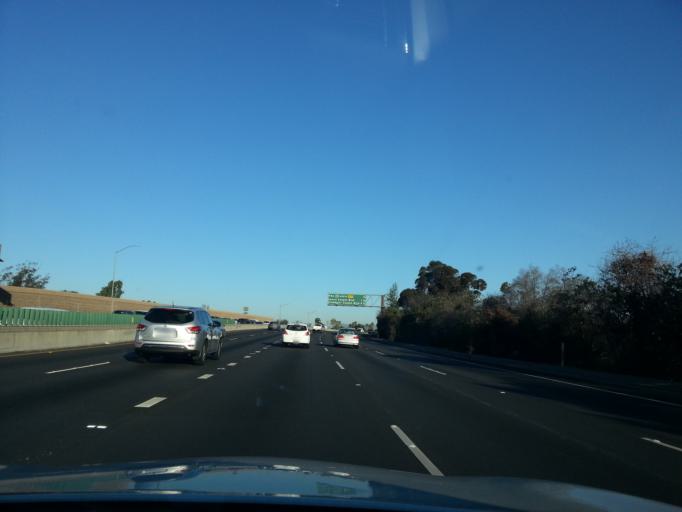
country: US
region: California
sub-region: Los Angeles County
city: Universal City
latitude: 34.1480
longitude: -118.3716
